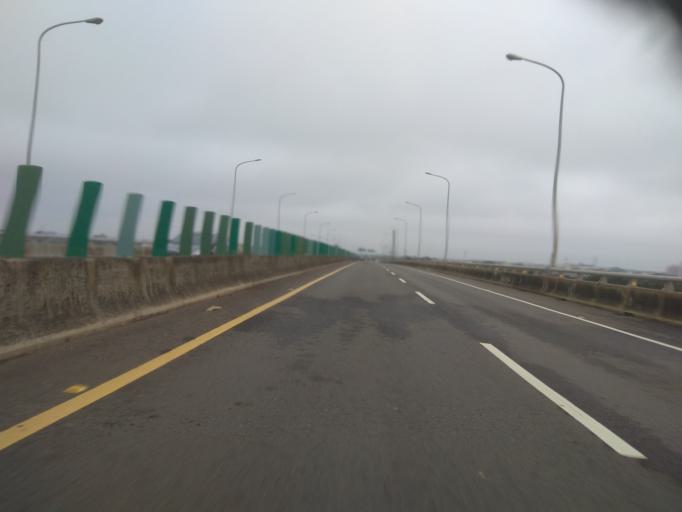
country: TW
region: Taiwan
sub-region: Hsinchu
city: Zhubei
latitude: 25.0006
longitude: 121.1000
